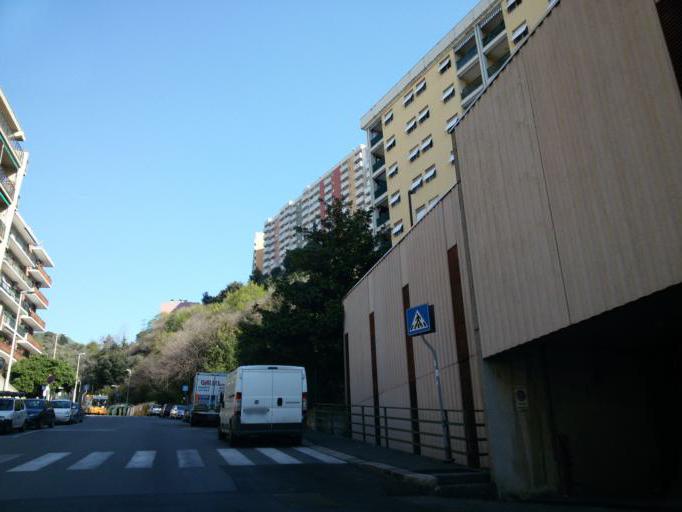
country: IT
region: Liguria
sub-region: Provincia di Genova
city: San Teodoro
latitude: 44.4209
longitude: 8.9095
